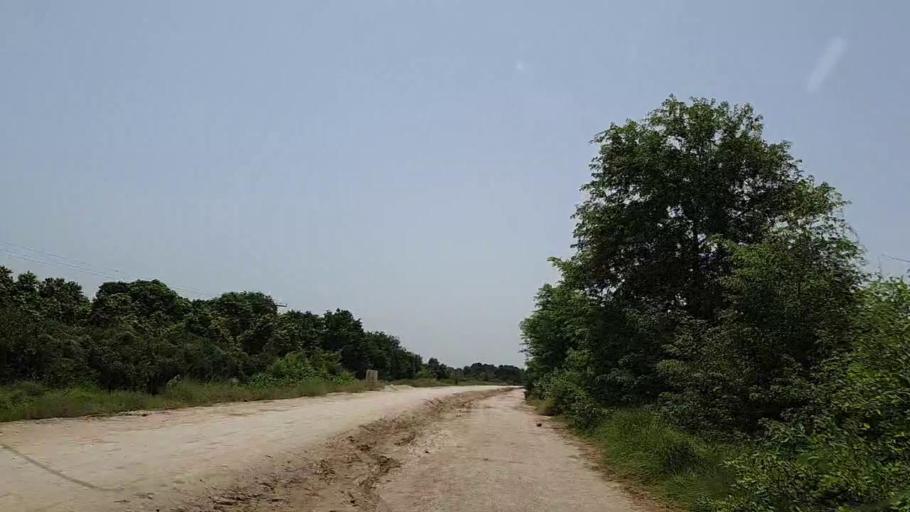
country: PK
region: Sindh
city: Tharu Shah
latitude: 26.9977
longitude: 68.1157
